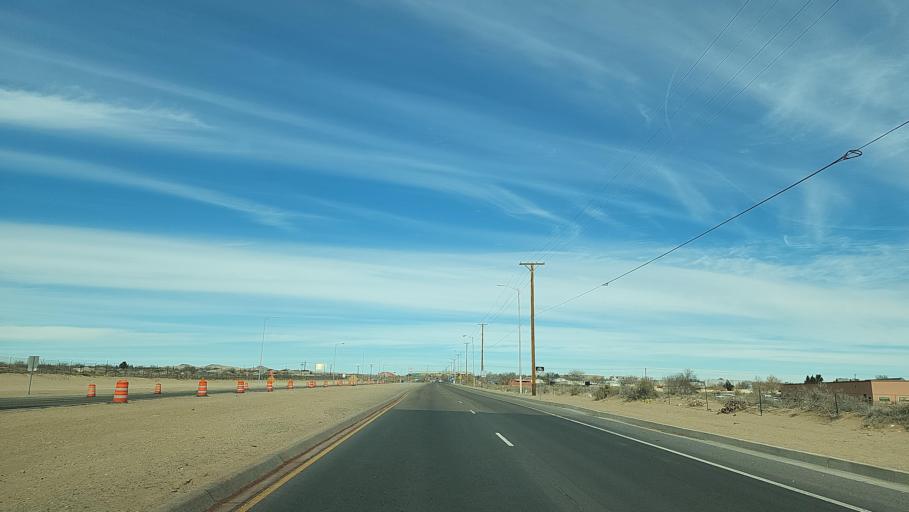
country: US
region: New Mexico
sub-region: Bernalillo County
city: Albuquerque
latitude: 35.0667
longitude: -106.7104
